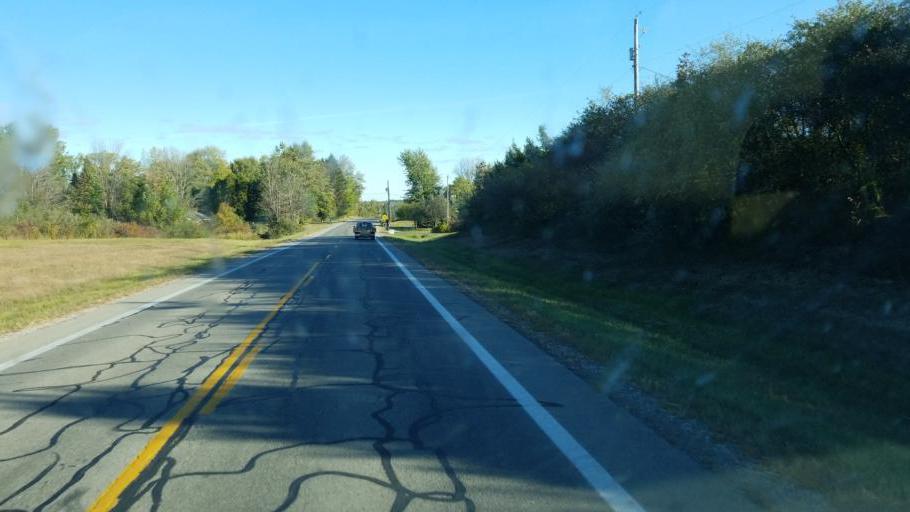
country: US
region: Ohio
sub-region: Crawford County
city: Galion
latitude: 40.6639
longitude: -82.8217
